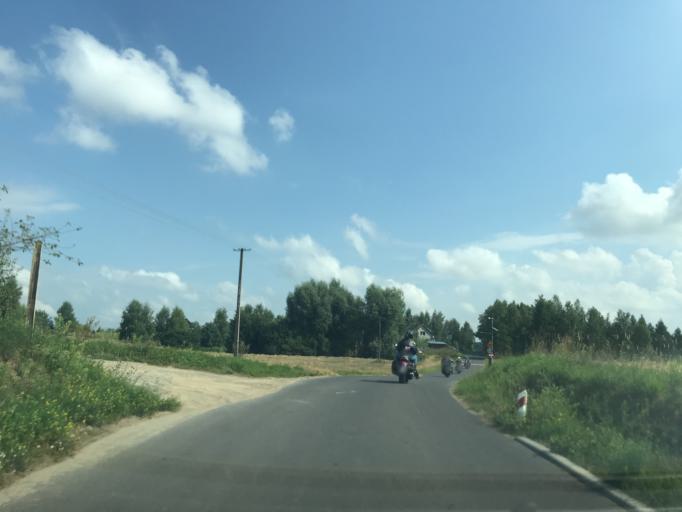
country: PL
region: Warmian-Masurian Voivodeship
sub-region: Powiat nowomiejski
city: Biskupiec
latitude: 53.4533
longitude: 19.4528
